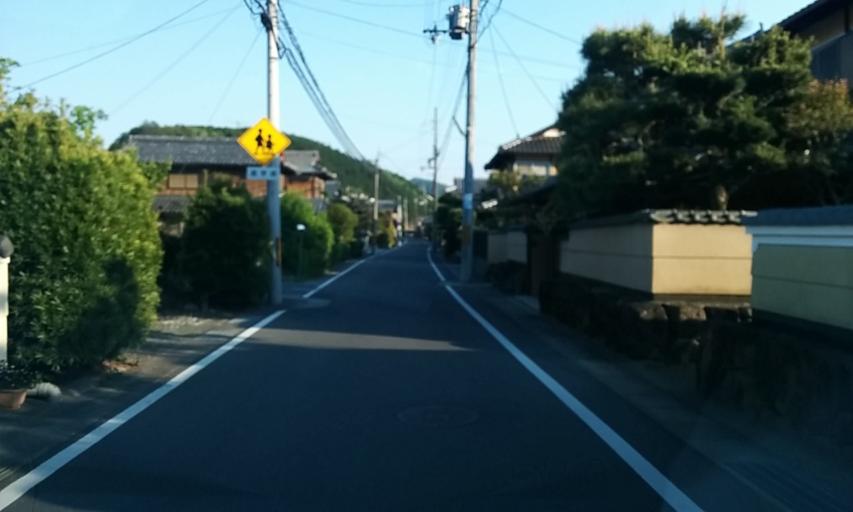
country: JP
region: Kyoto
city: Kameoka
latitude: 35.0901
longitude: 135.5105
